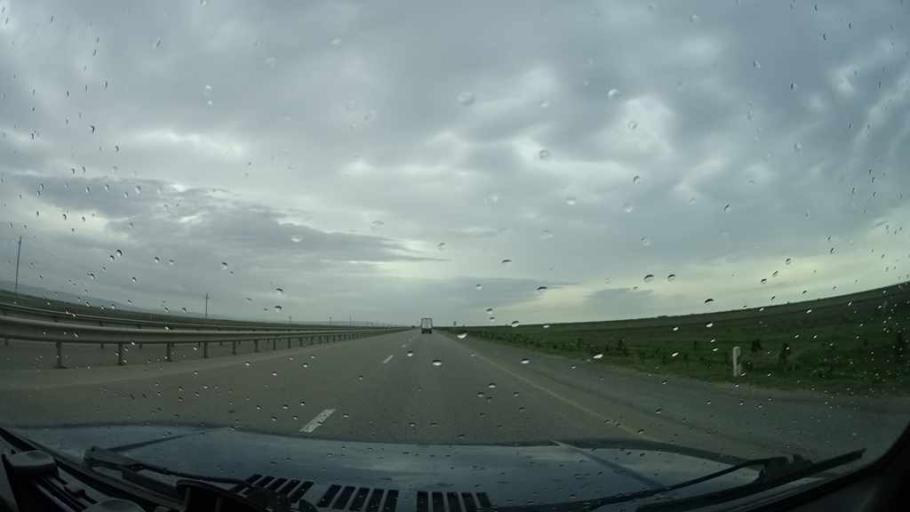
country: AZ
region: Goranboy
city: Goranboy
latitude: 40.6440
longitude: 46.7084
